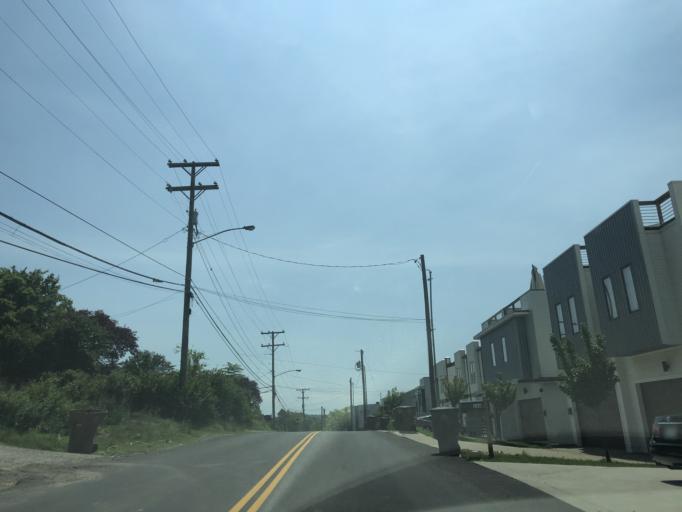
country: US
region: Tennessee
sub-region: Davidson County
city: Nashville
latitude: 36.1954
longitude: -86.7743
